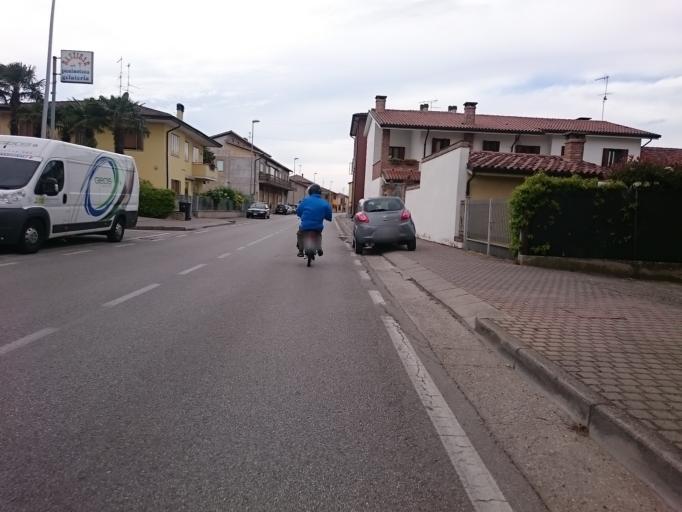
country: IT
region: Veneto
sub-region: Provincia di Padova
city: Sant'Elena
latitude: 45.1827
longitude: 11.7136
